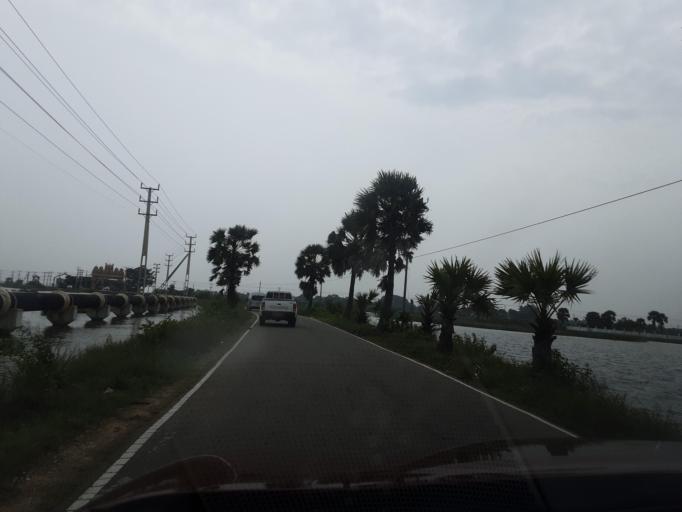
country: LK
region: Northern Province
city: Jaffna
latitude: 9.6644
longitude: 80.0595
